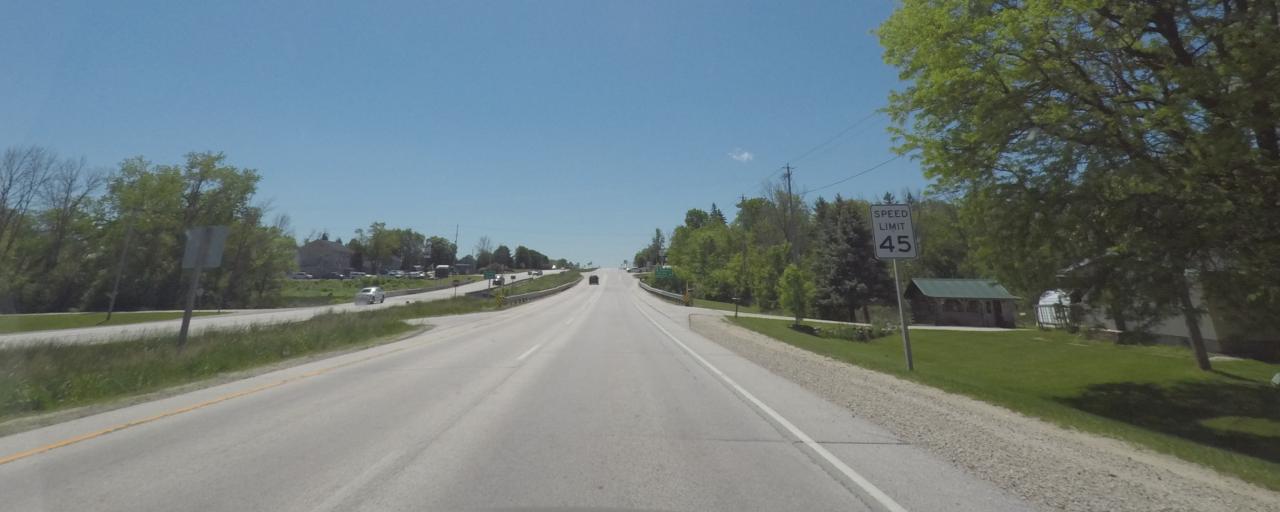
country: US
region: Wisconsin
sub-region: Sheboygan County
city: Plymouth
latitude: 43.6767
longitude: -87.9409
